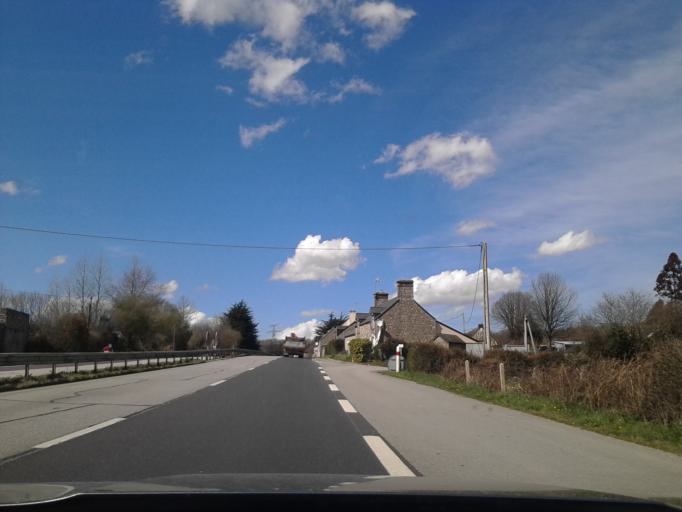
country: FR
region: Lower Normandy
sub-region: Departement de la Manche
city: Brix
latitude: 49.5420
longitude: -1.5476
